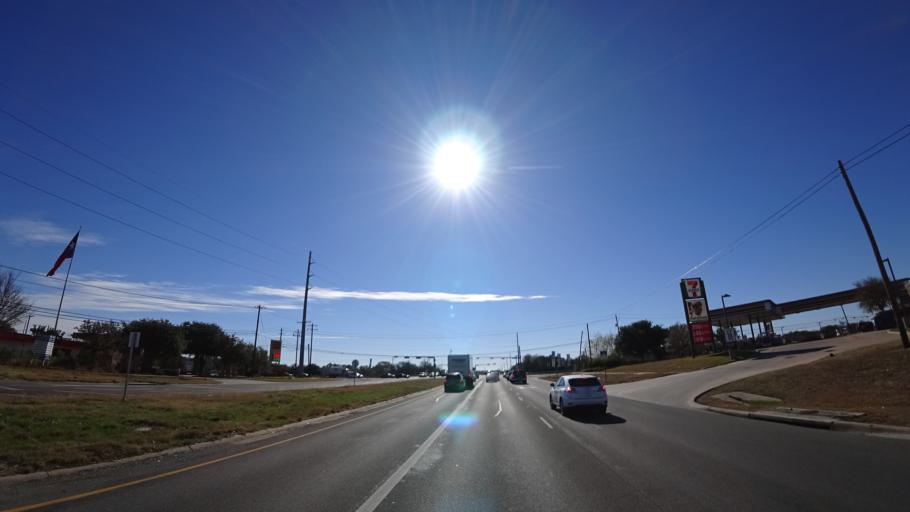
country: US
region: Texas
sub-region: Williamson County
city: Jollyville
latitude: 30.4778
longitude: -97.7655
